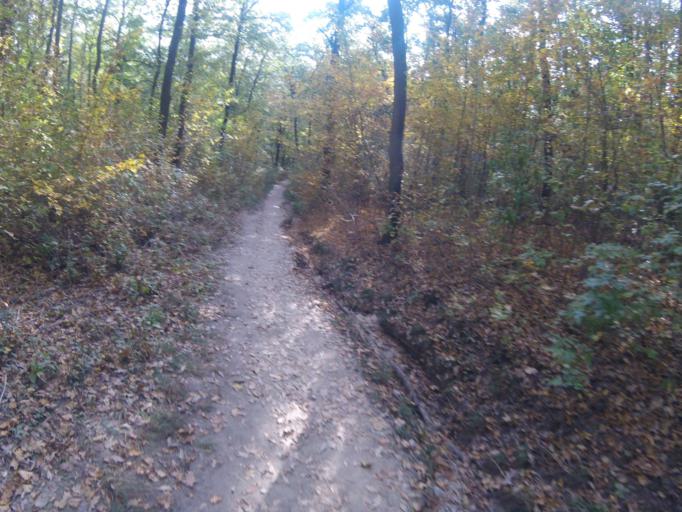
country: HU
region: Fejer
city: Bodajk
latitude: 47.3094
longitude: 18.2257
